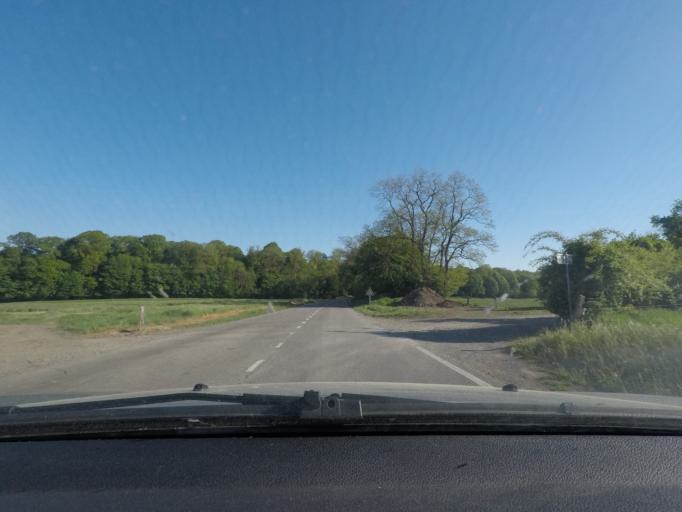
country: BE
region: Wallonia
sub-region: Province de Namur
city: Rochefort
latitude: 50.2140
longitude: 5.1483
